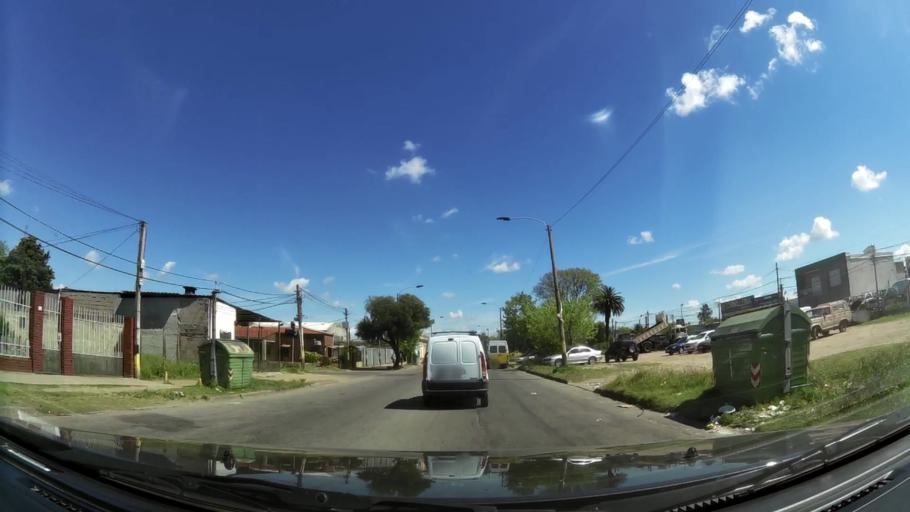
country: UY
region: Montevideo
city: Montevideo
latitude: -34.8479
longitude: -56.1341
